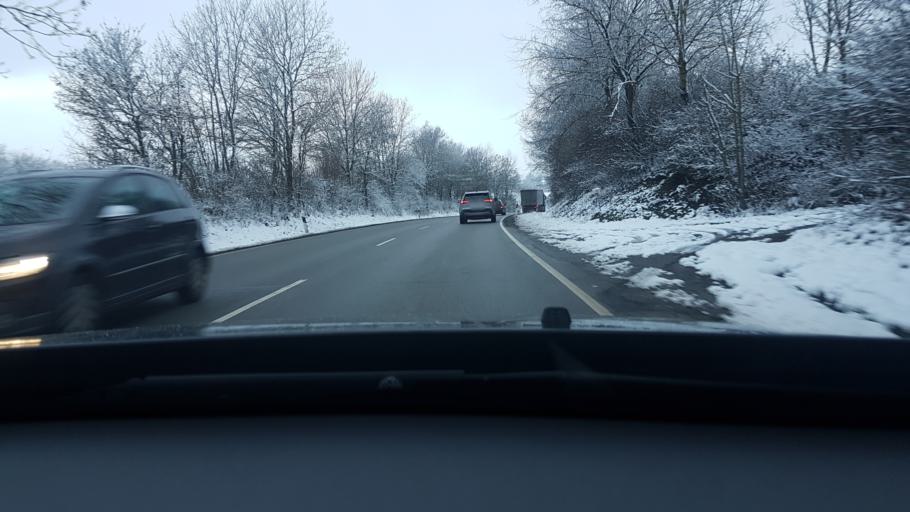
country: DE
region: Hesse
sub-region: Regierungsbezirk Kassel
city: Korbach
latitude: 51.3185
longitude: 8.8447
